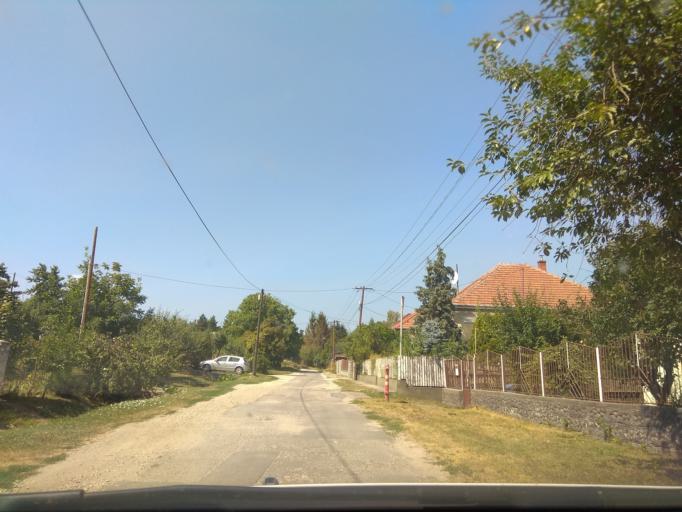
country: HU
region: Borsod-Abauj-Zemplen
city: Miskolc
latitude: 48.0656
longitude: 20.7779
